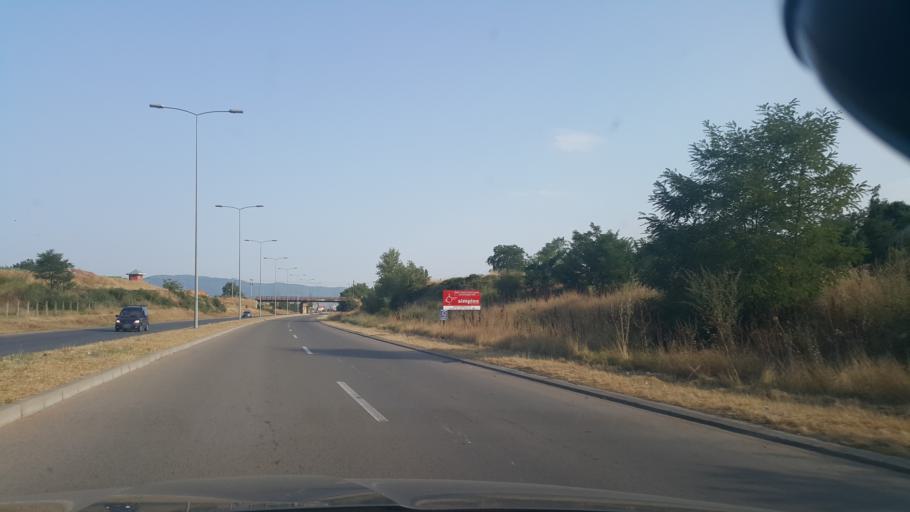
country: RS
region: Central Serbia
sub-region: Nisavski Okrug
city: Nis
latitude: 43.3219
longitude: 21.8268
